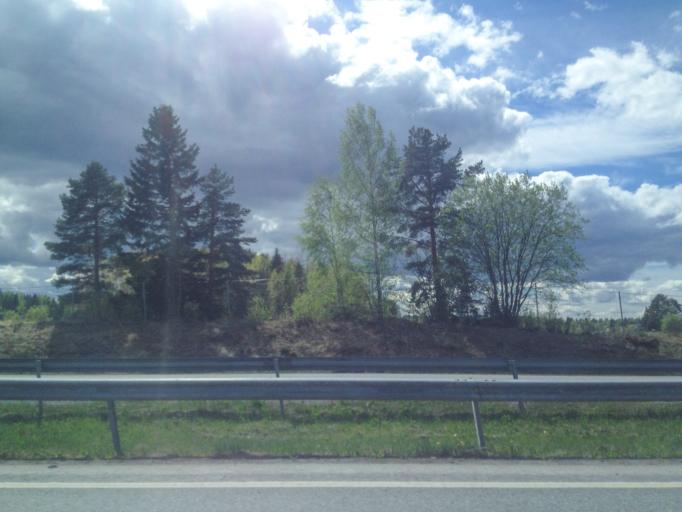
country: FI
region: Pirkanmaa
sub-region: Etelae-Pirkanmaa
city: Akaa
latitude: 61.1902
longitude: 23.8714
